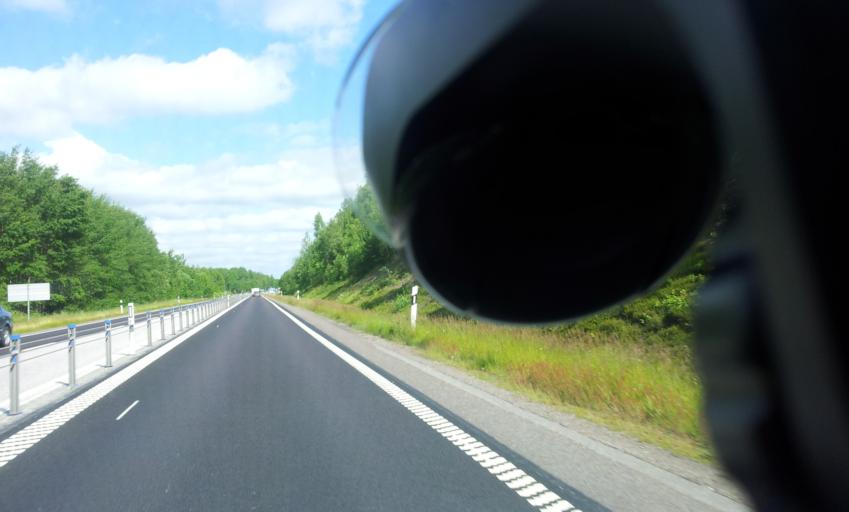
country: SE
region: OEstergoetland
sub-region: Soderkopings Kommun
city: Soederkoeping
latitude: 58.5050
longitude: 16.2973
